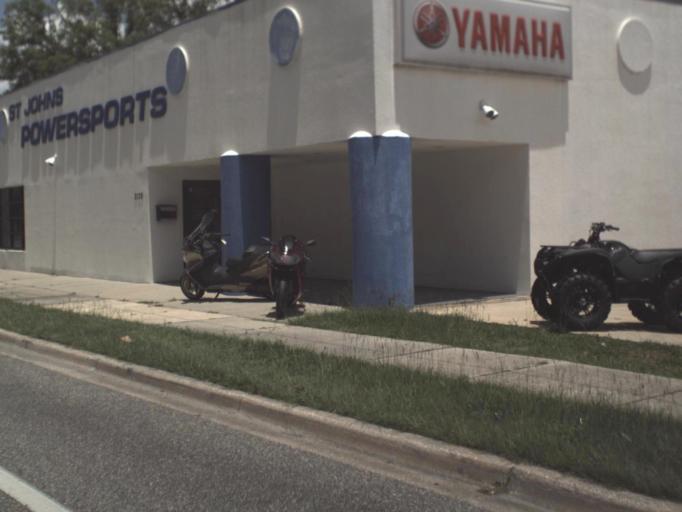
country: US
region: Florida
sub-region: Putnam County
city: Palatka
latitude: 29.6512
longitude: -81.6517
